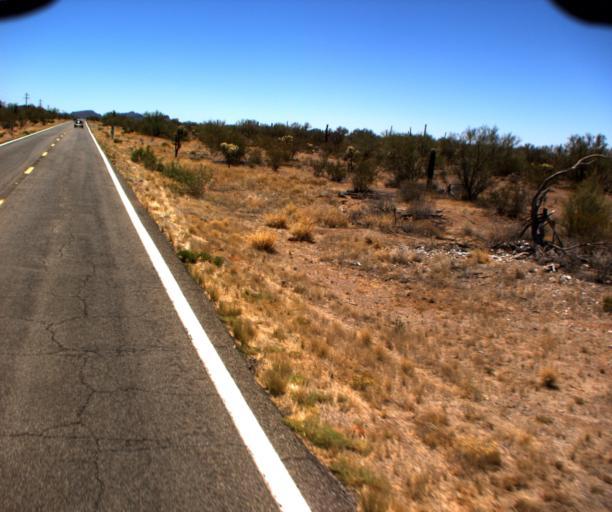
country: US
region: Arizona
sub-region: Pima County
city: Sells
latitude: 32.0307
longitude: -112.0099
